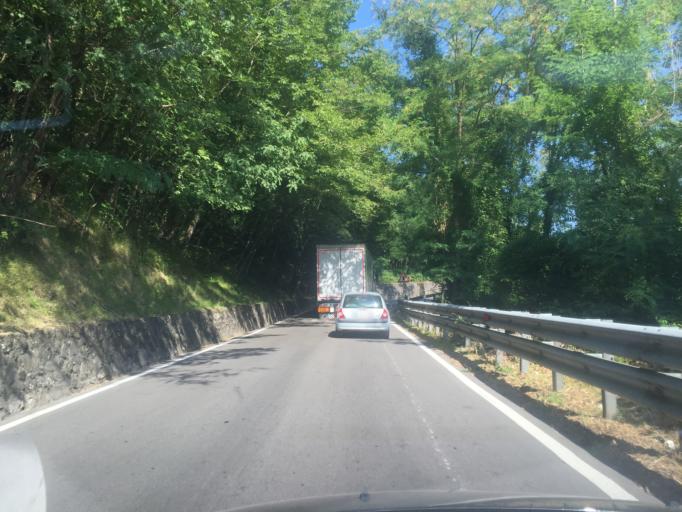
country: IT
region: Tuscany
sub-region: Provincia di Lucca
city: San Romano in Garfagnana
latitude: 44.1448
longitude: 10.3574
